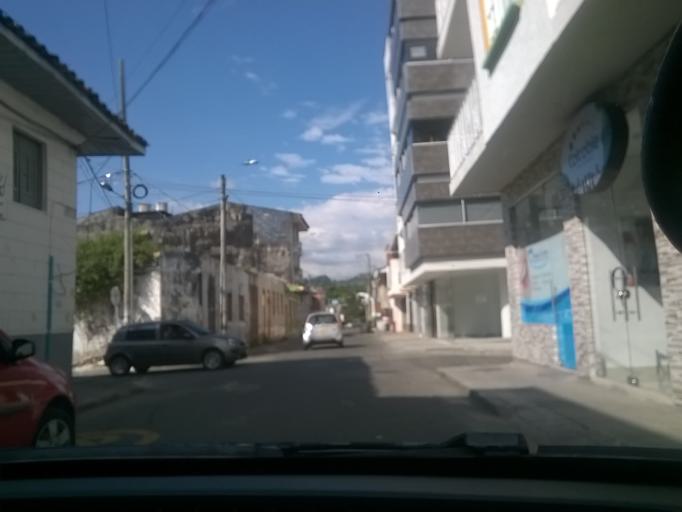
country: CO
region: Quindio
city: Calarca
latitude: 4.5321
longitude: -75.6397
